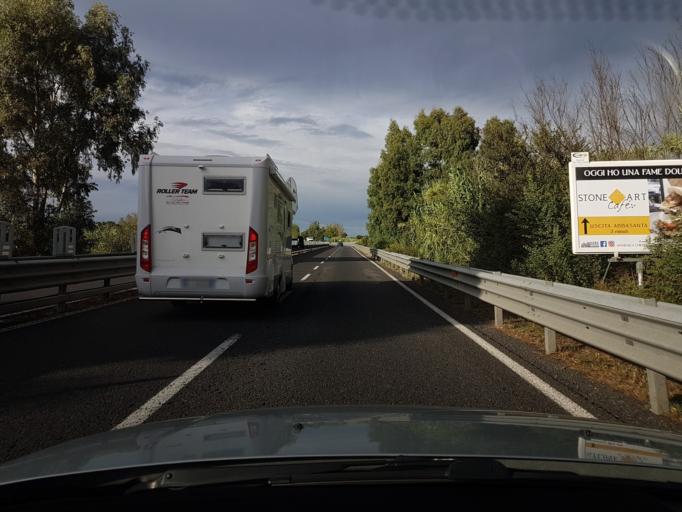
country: IT
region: Sardinia
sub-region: Provincia di Oristano
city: Paulilatino
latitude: 40.1060
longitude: 8.7899
